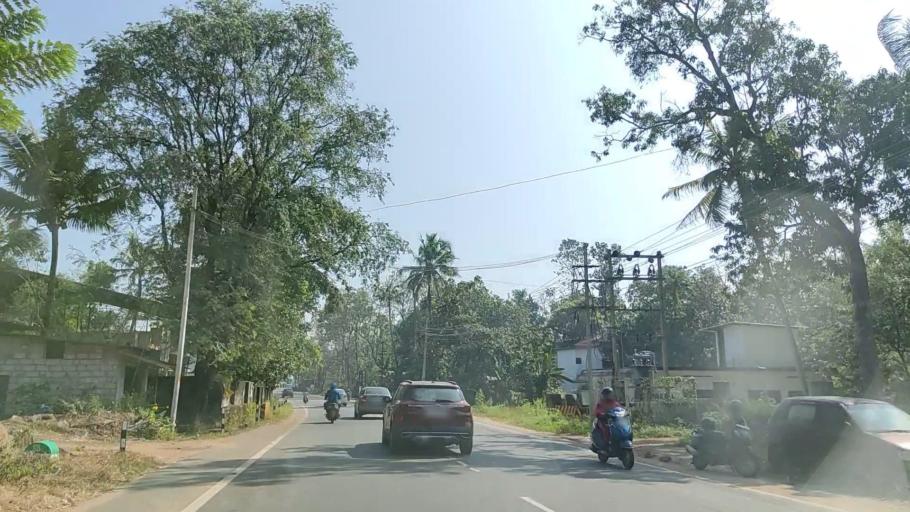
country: IN
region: Kerala
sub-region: Kollam
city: Punalur
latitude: 8.9322
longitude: 76.9352
